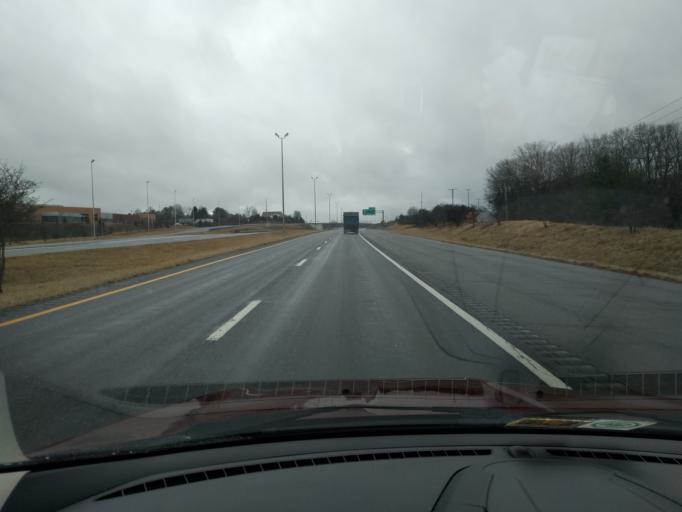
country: US
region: Virginia
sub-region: Montgomery County
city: Merrimac
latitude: 37.1981
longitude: -80.4100
